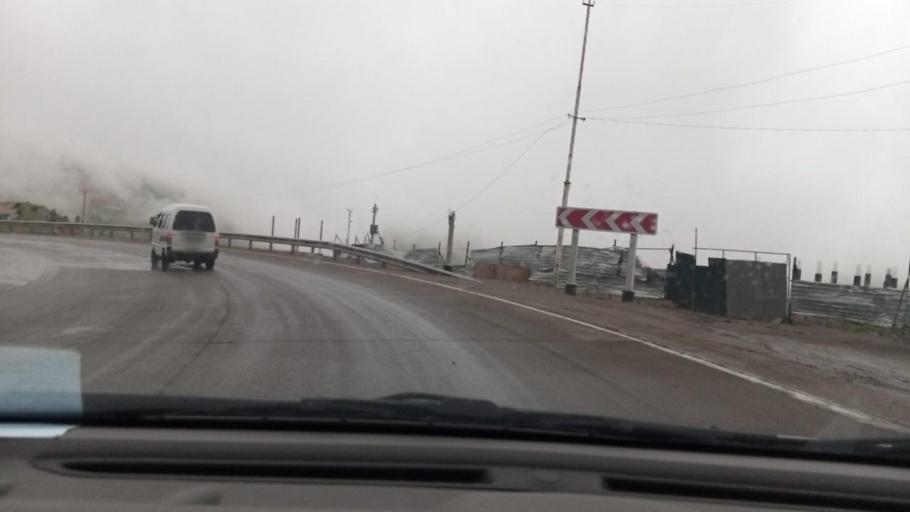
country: UZ
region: Toshkent
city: Angren
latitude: 41.1141
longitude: 70.5039
